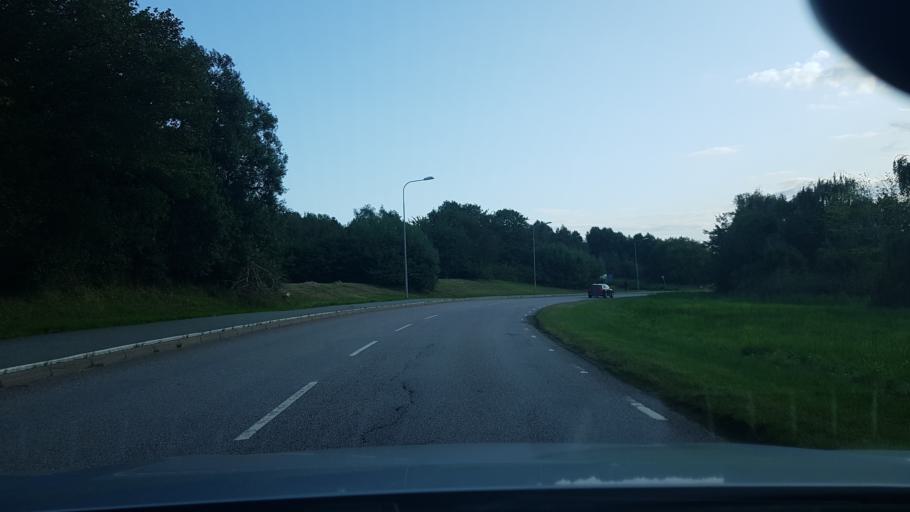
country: SE
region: Vaestra Goetaland
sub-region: Goteborg
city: Majorna
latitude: 57.6468
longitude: 11.8682
